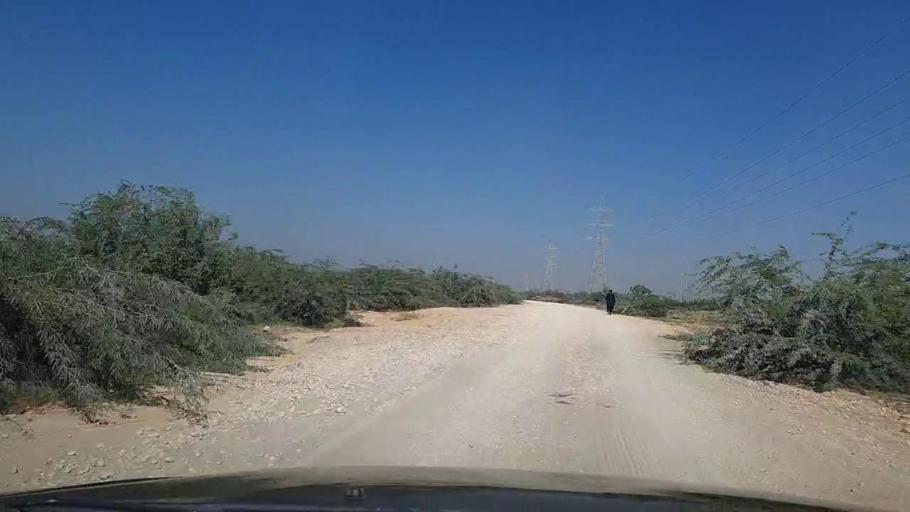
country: PK
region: Sindh
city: Thatta
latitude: 24.6276
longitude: 67.8342
